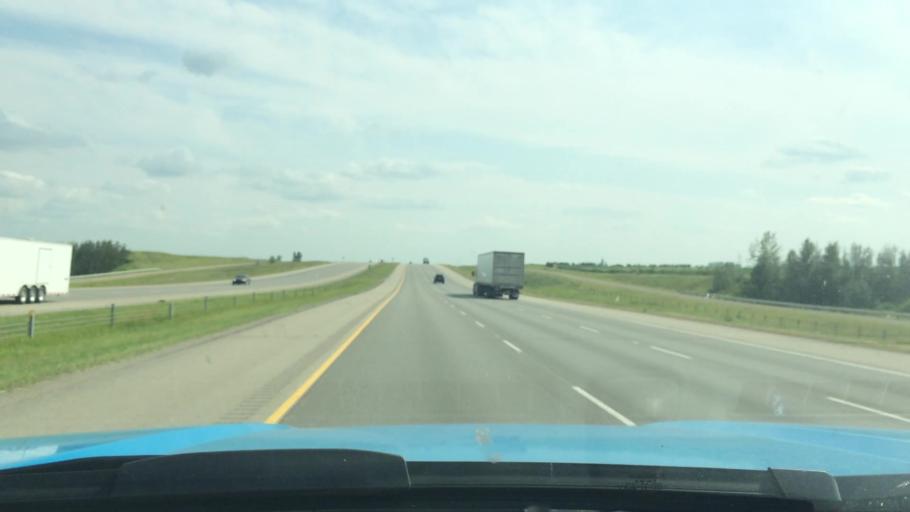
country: CA
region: Alberta
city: Crossfield
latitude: 51.5164
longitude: -114.0258
